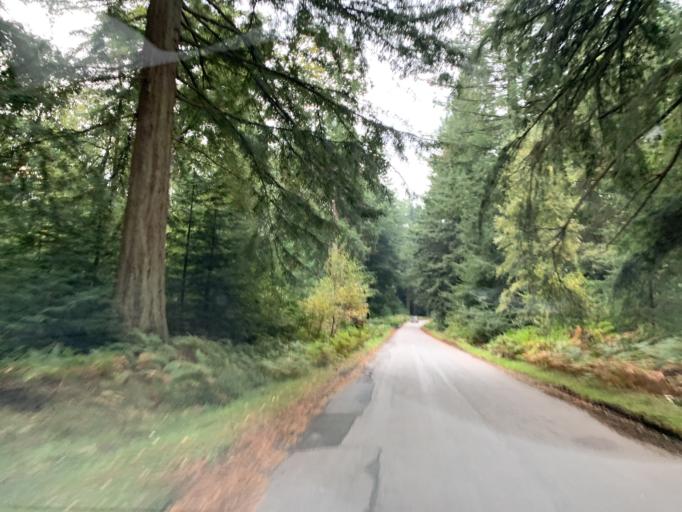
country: GB
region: England
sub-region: Hampshire
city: Lyndhurst
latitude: 50.8456
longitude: -1.6221
